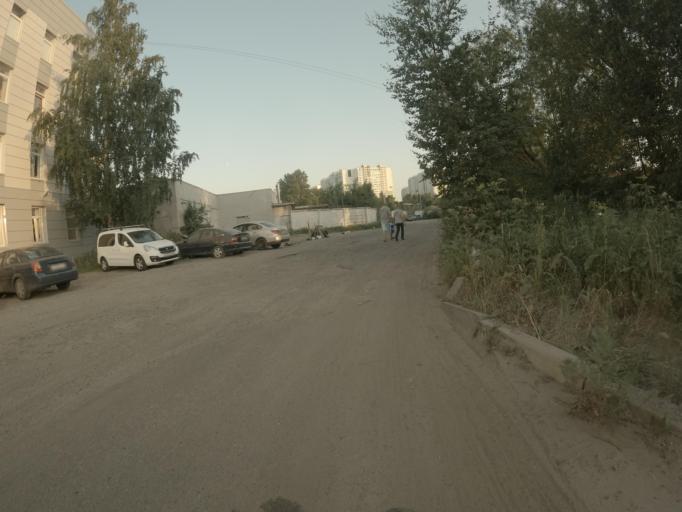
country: RU
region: St.-Petersburg
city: Krasnogvargeisky
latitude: 59.9431
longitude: 30.4400
